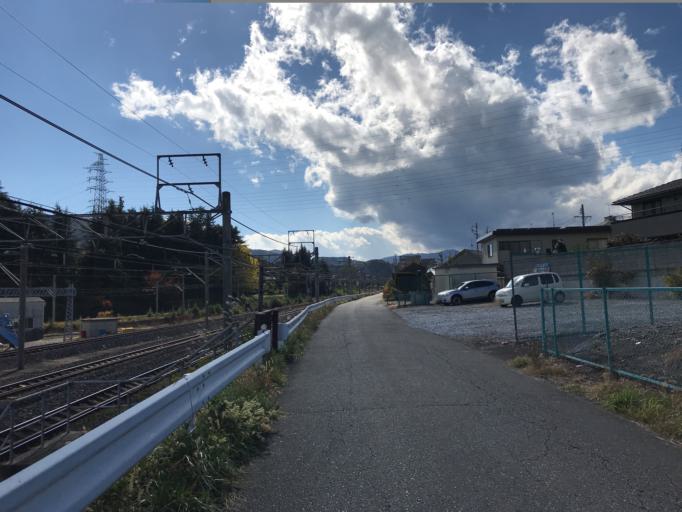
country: JP
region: Nagano
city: Shiojiri
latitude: 36.1125
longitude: 137.9467
